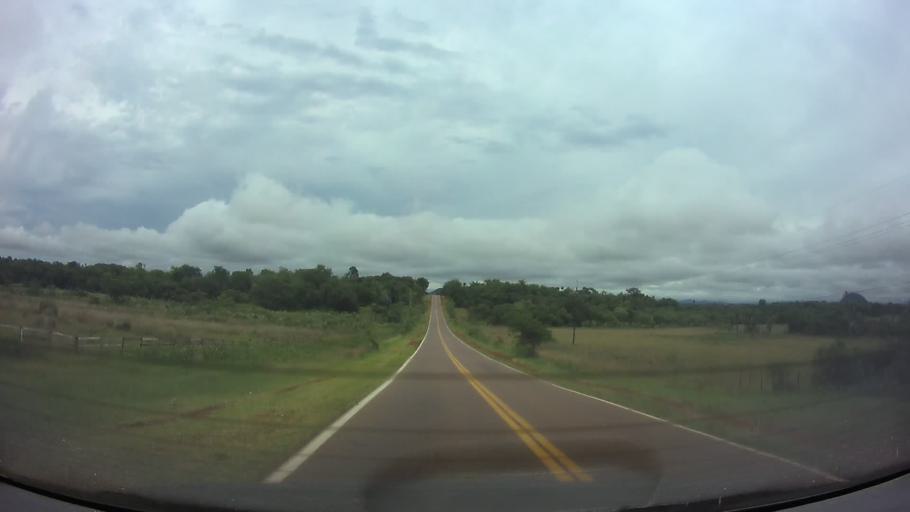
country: PY
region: Paraguari
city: Acahay
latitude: -25.8542
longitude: -57.1390
